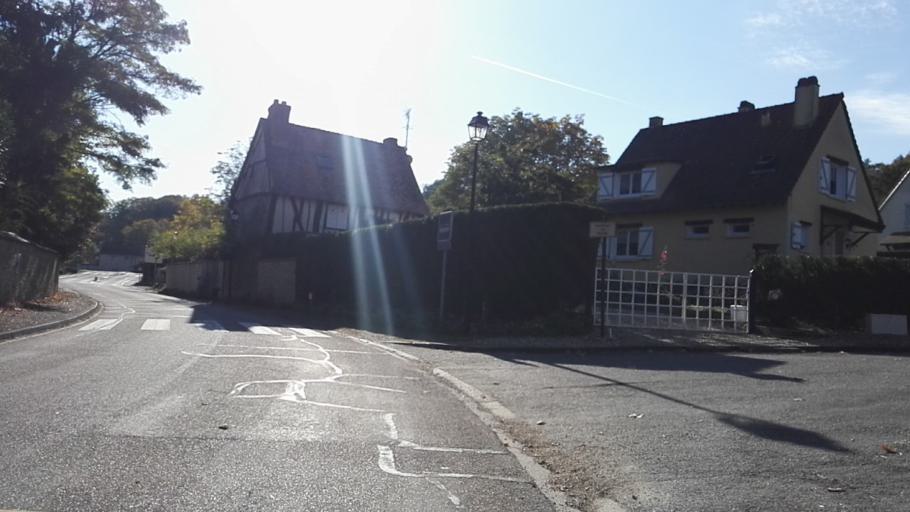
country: FR
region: Haute-Normandie
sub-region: Departement de l'Eure
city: Menilles
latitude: 49.0298
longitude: 1.3439
